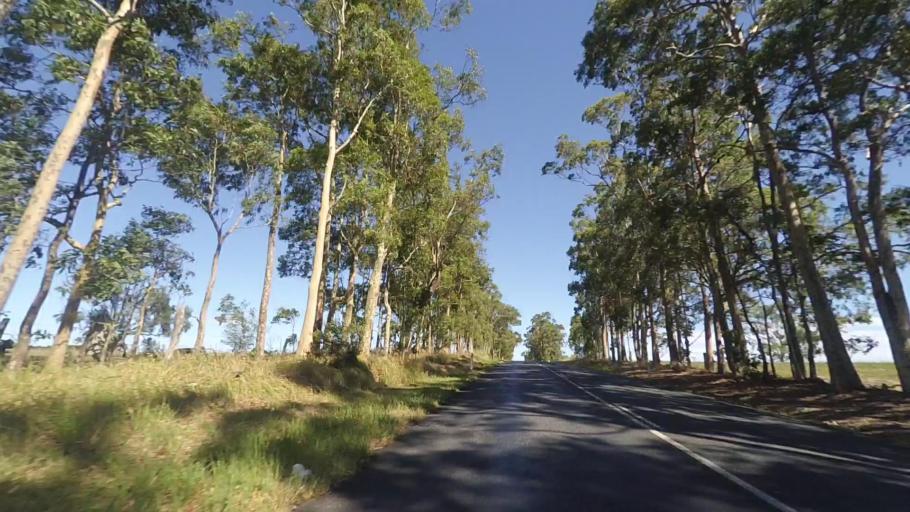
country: AU
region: New South Wales
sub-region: Great Lakes
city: Hawks Nest
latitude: -32.6239
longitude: 152.1289
